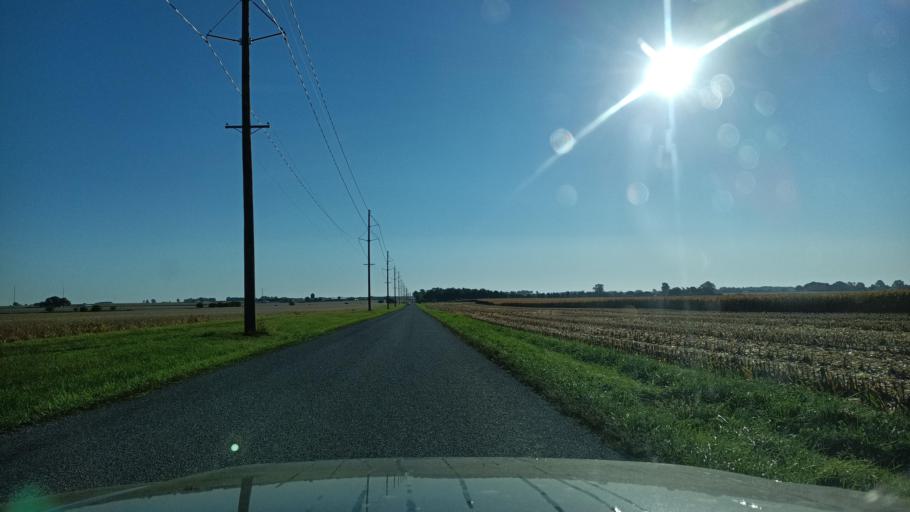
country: US
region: Illinois
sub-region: Champaign County
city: Savoy
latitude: 40.0544
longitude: -88.2251
